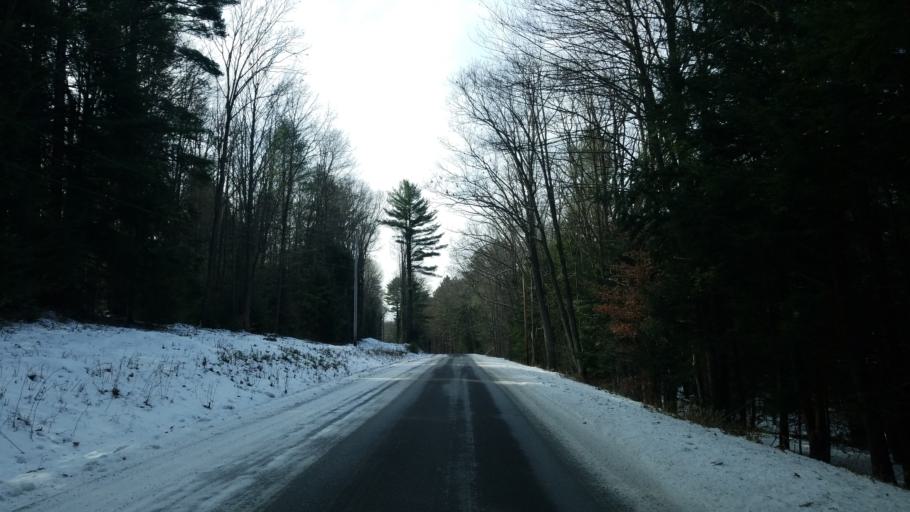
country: US
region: Pennsylvania
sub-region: Clearfield County
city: Clearfield
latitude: 41.1898
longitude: -78.5198
